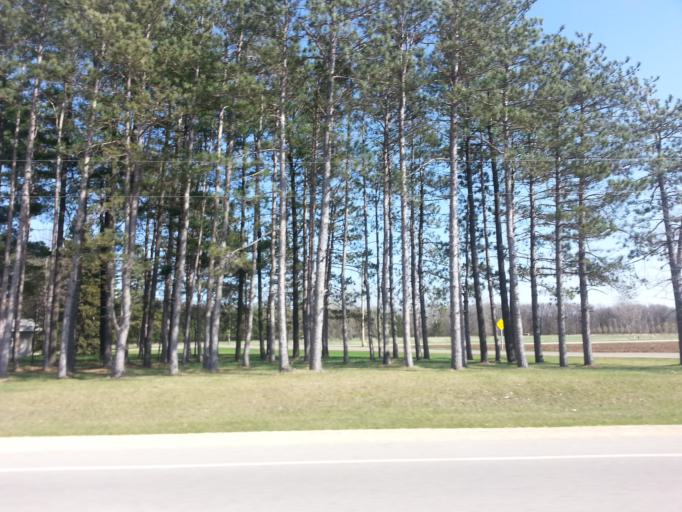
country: US
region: Wisconsin
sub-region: Pepin County
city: Durand
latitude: 44.6548
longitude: -91.9767
